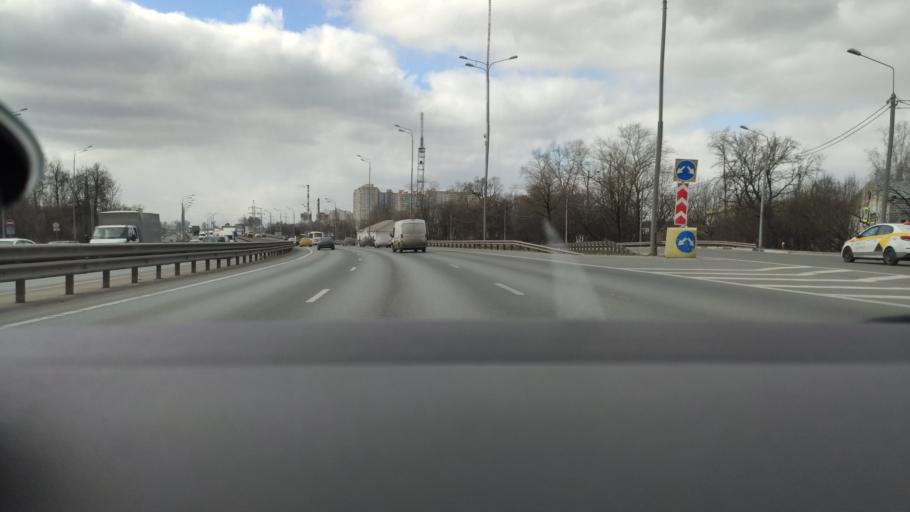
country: RU
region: Moskovskaya
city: Saltykovka
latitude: 55.7938
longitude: 37.9069
